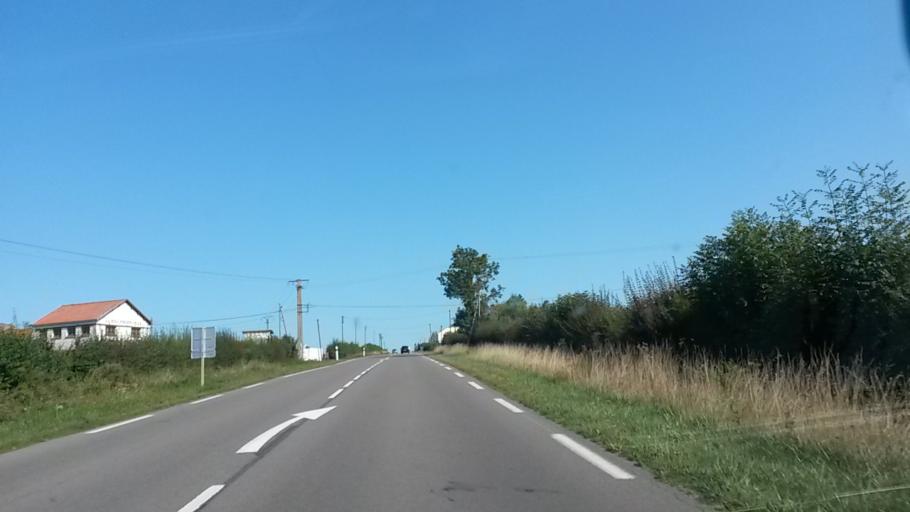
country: FR
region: Nord-Pas-de-Calais
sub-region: Departement du Nord
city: Avesnes-sur-Helpe
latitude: 50.0744
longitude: 3.9291
